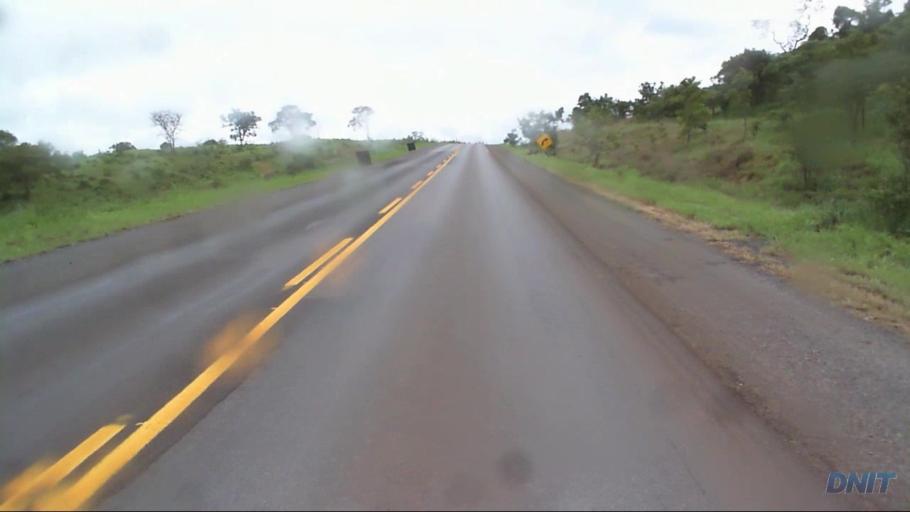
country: BR
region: Goias
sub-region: Padre Bernardo
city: Padre Bernardo
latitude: -15.1844
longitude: -48.4309
